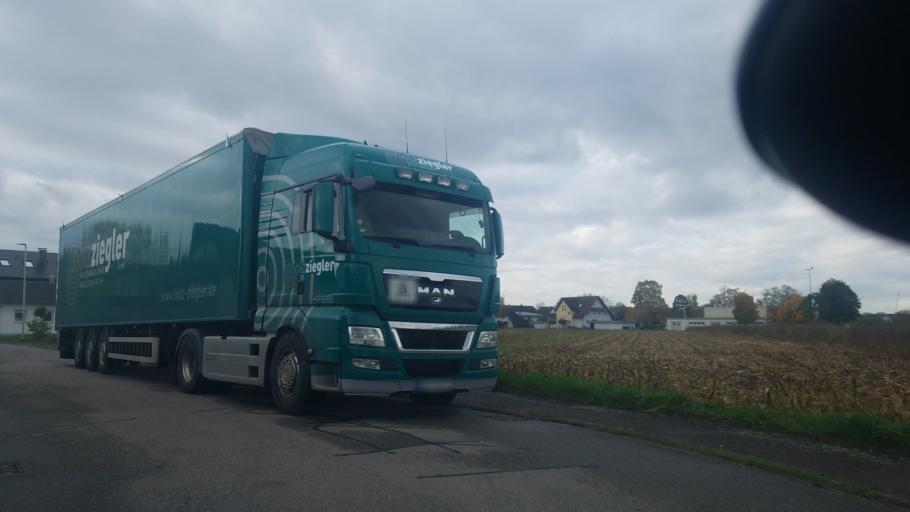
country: DE
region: Baden-Wuerttemberg
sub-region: Karlsruhe Region
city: Zell
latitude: 48.6577
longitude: 8.0254
